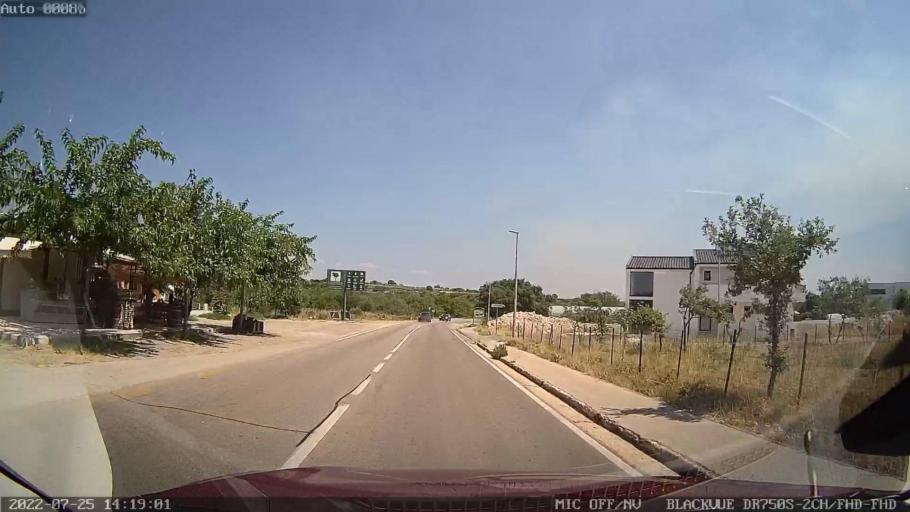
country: HR
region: Zadarska
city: Zadar
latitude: 44.1793
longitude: 15.2841
